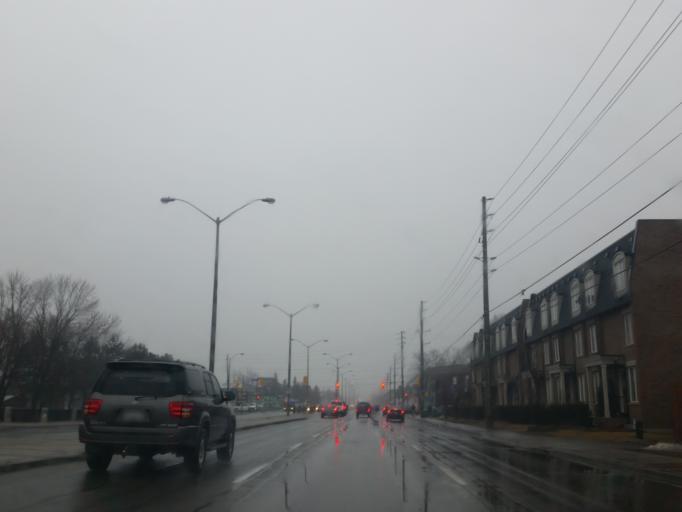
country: CA
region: Ontario
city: Scarborough
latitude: 43.7631
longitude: -79.1939
